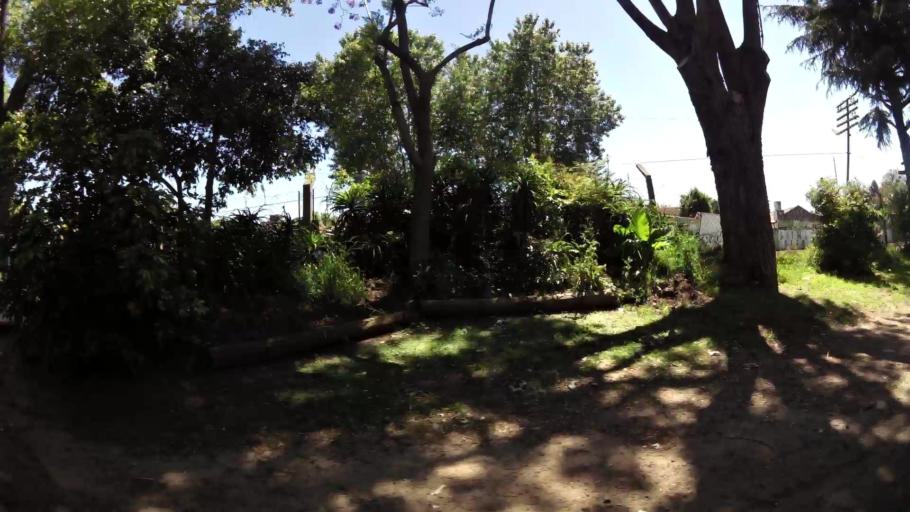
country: AR
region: Buenos Aires
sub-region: Partido de General San Martin
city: General San Martin
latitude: -34.5283
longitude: -58.5403
